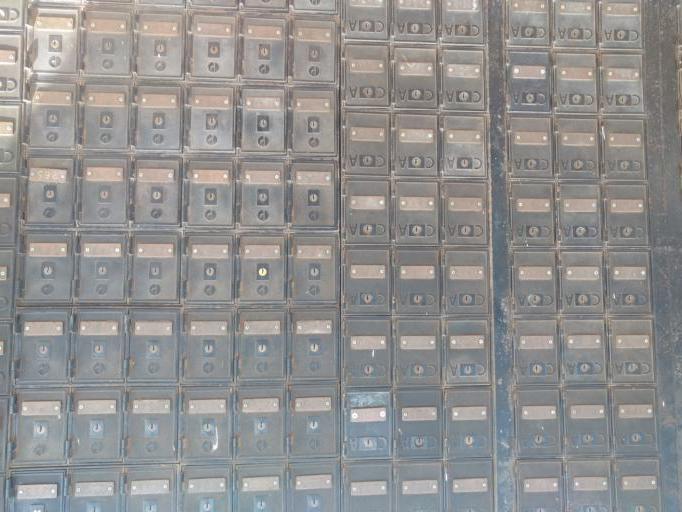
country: AU
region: South Australia
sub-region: Mid Murray
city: Mannum
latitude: -34.9134
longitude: 139.3124
